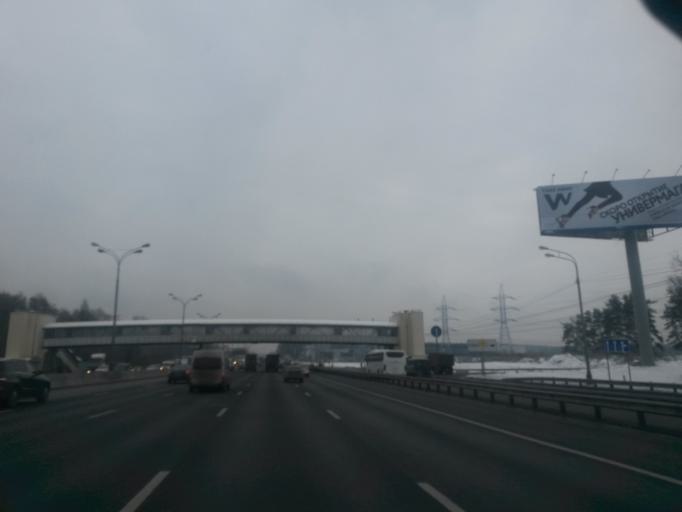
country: RU
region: Moskovskaya
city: Vostryakovo
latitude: 55.6580
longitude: 37.4385
